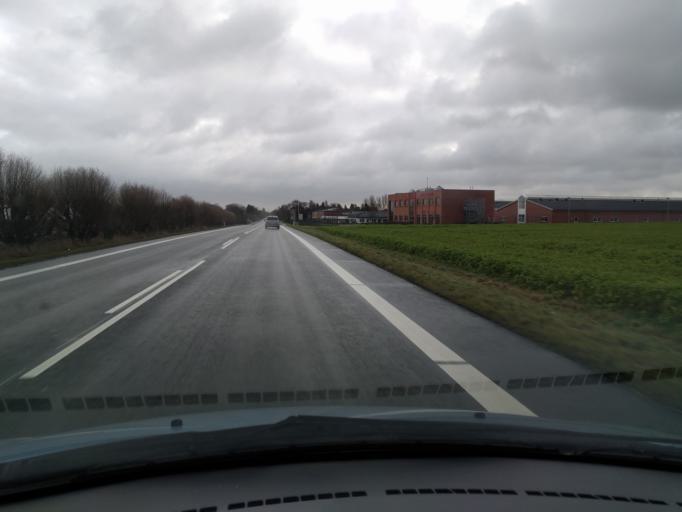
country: DK
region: South Denmark
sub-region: Kerteminde Kommune
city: Langeskov
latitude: 55.3765
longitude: 10.5528
